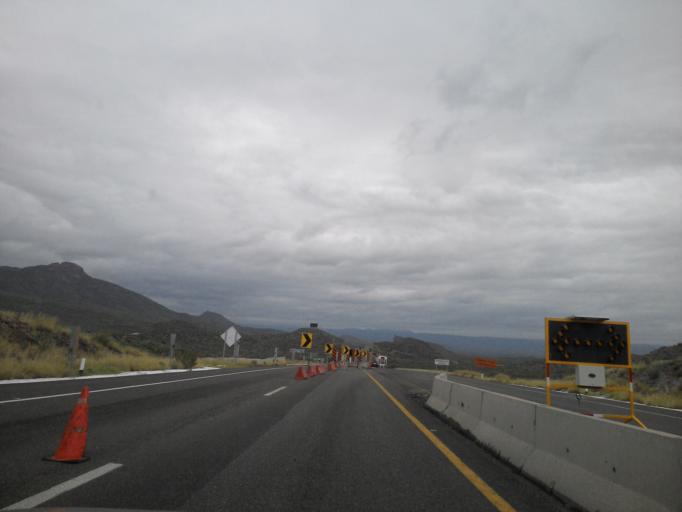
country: MX
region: Durango
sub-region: Lerdo
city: Sapioris
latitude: 25.1694
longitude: -103.7233
